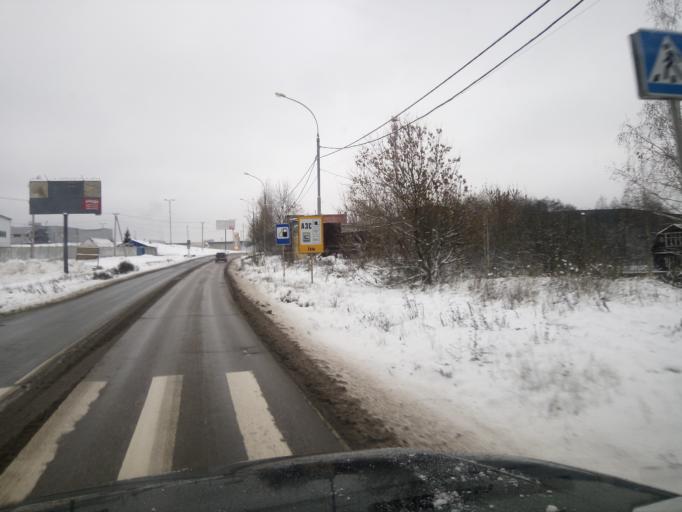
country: RU
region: Moskovskaya
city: Skhodnya
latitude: 55.9684
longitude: 37.3101
